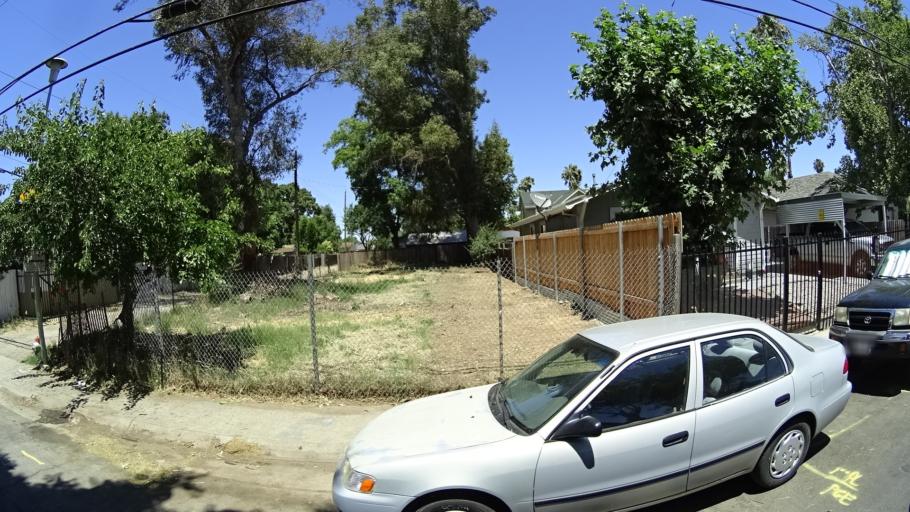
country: US
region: California
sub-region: Sacramento County
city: Parkway
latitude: 38.5376
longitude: -121.4669
